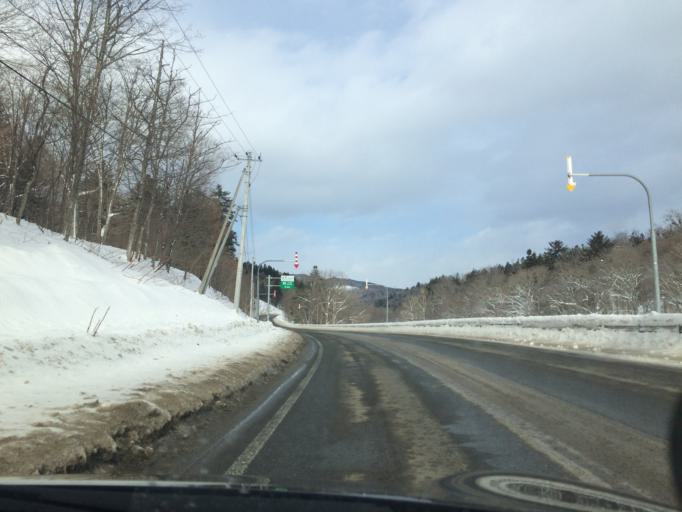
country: JP
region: Hokkaido
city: Shimo-furano
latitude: 42.9625
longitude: 142.3751
